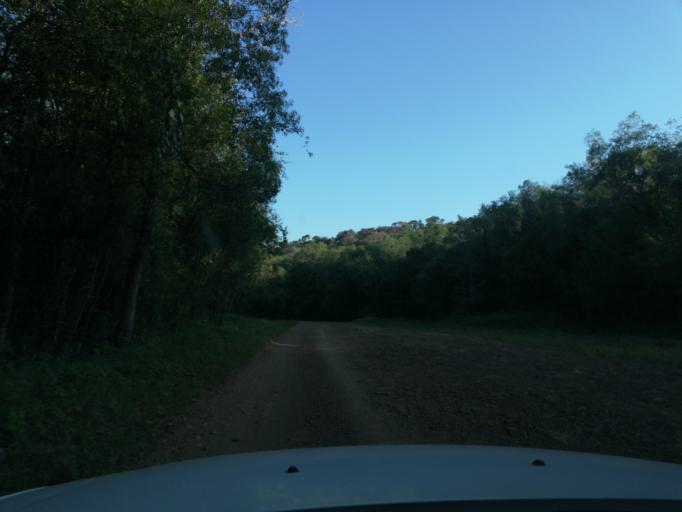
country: AR
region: Misiones
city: Cerro Cora
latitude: -27.6139
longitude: -55.7060
